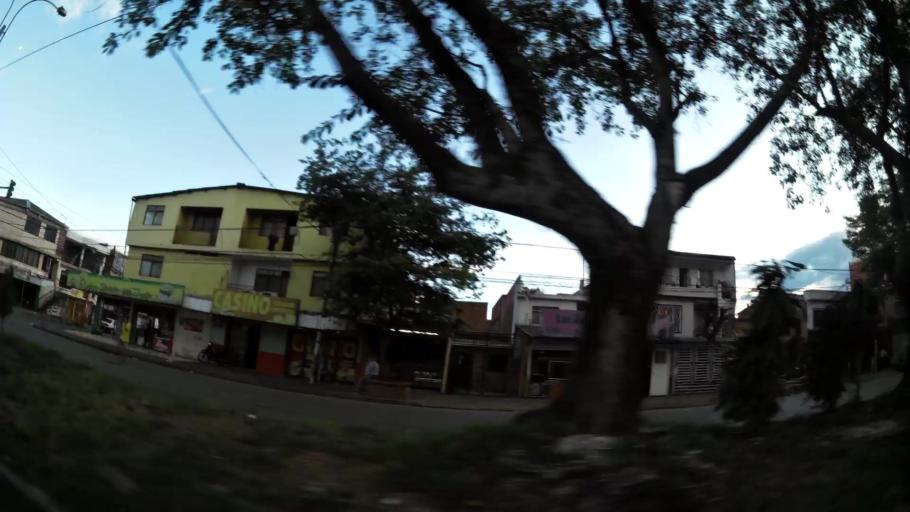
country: CO
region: Valle del Cauca
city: Cali
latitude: 3.4290
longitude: -76.5186
